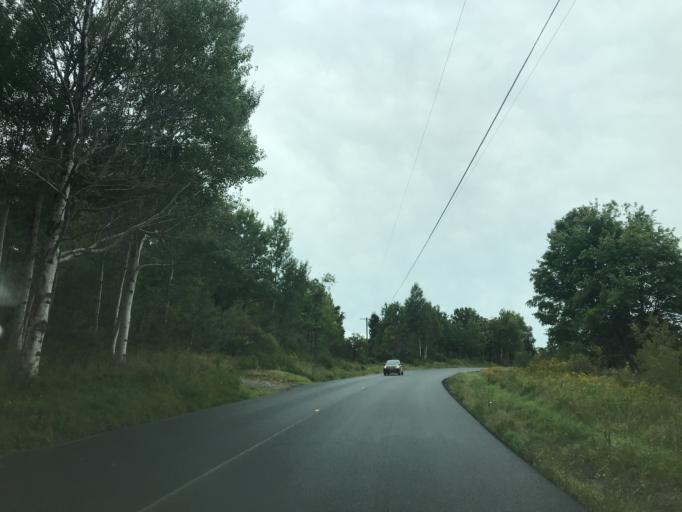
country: US
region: New York
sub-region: Delaware County
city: Stamford
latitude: 42.5214
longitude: -74.6223
